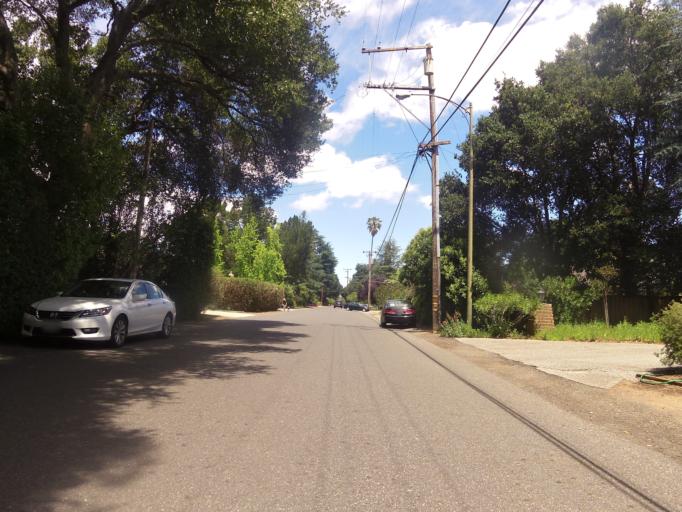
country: US
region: California
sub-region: Santa Clara County
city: Loyola
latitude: 37.3539
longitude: -122.0835
